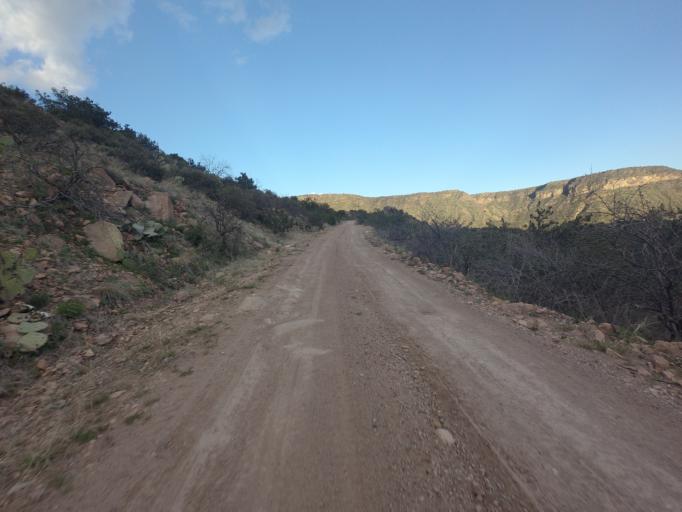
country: US
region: Arizona
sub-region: Gila County
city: Pine
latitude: 34.3706
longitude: -111.6681
